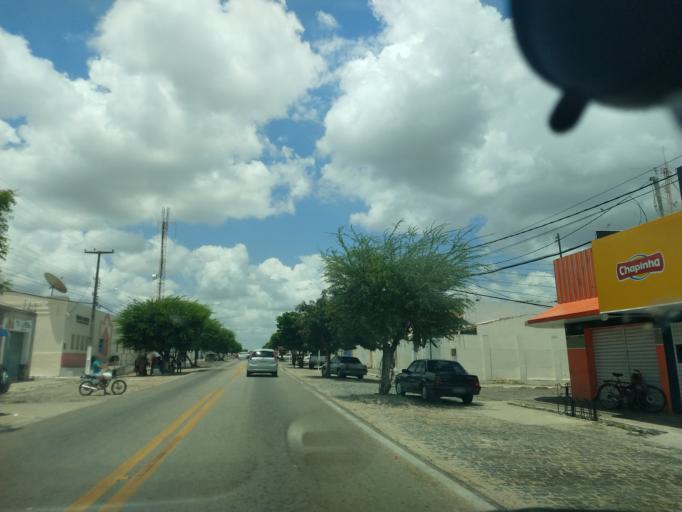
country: BR
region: Rio Grande do Norte
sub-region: Tangara
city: Tangara
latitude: -6.2002
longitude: -35.8017
